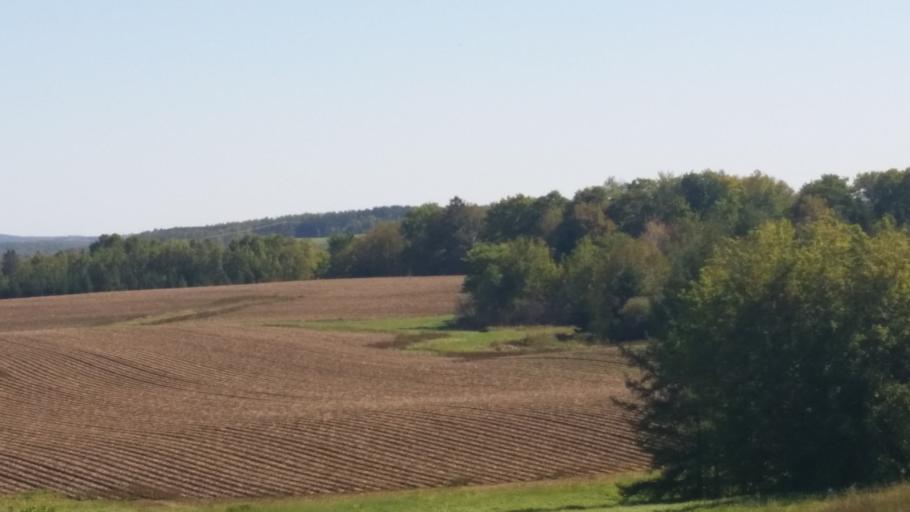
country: US
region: Maine
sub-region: Aroostook County
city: Easton
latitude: 46.5430
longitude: -67.9178
